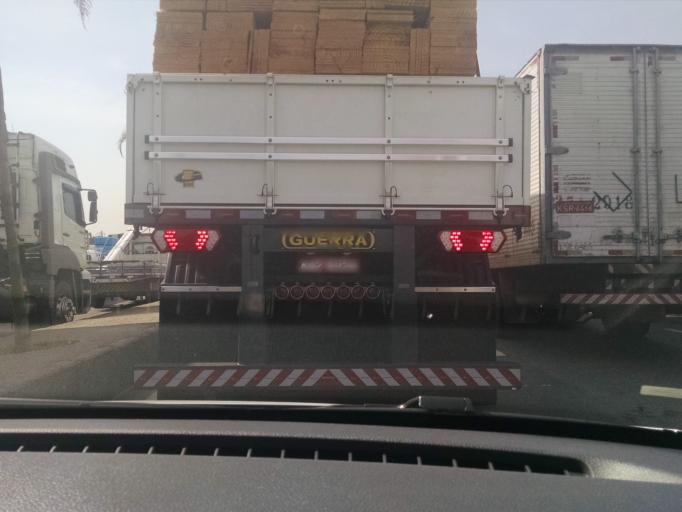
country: BR
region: Rio de Janeiro
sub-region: Duque De Caxias
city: Duque de Caxias
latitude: -22.8150
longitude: -43.2980
